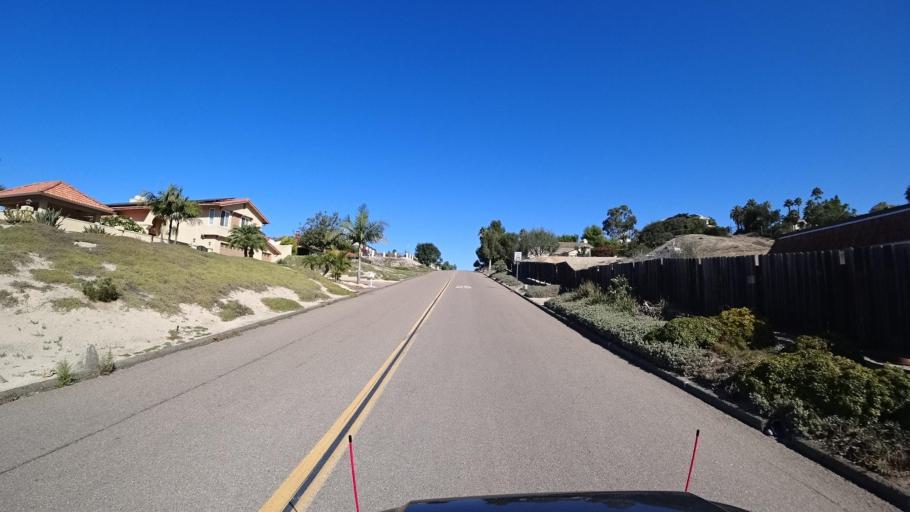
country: US
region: California
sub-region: San Diego County
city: Bonita
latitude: 32.6593
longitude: -117.0152
